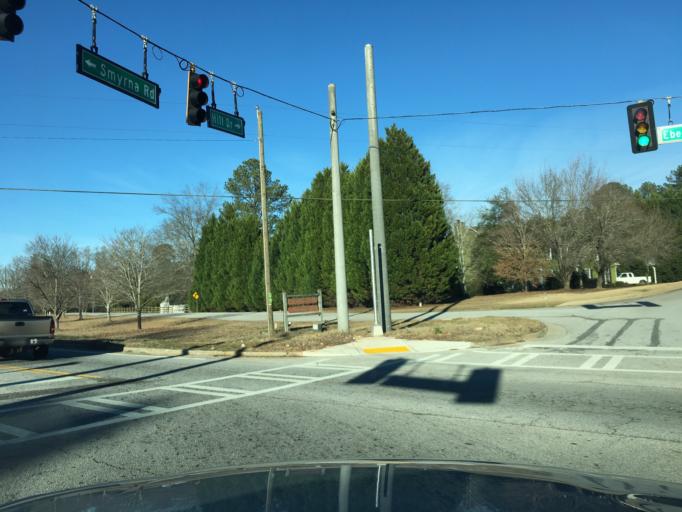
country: US
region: Georgia
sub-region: Rockdale County
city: Conyers
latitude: 33.6529
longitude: -84.0501
